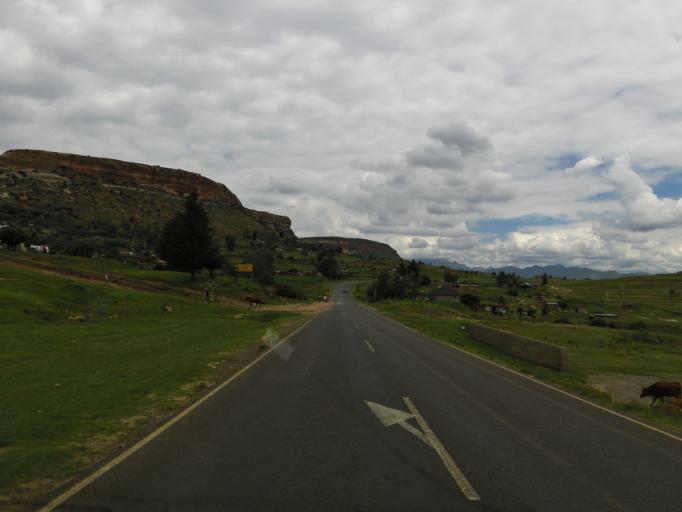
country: LS
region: Leribe
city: Leribe
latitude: -28.9410
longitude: 28.1687
